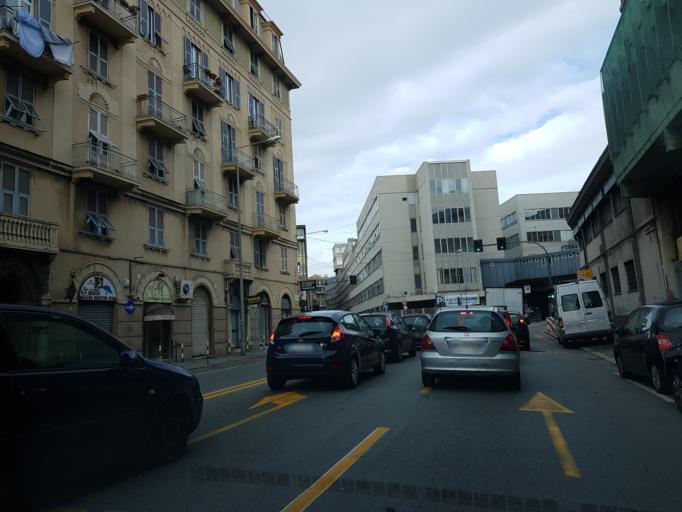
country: IT
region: Liguria
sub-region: Provincia di Genova
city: San Teodoro
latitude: 44.4218
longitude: 8.8566
